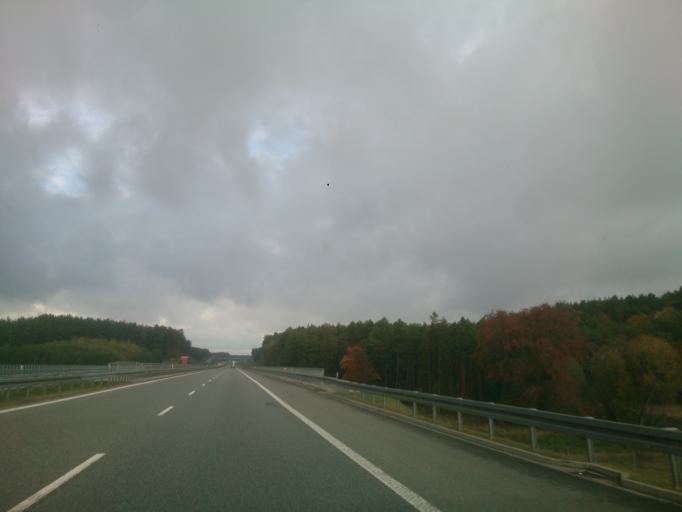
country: PL
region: Pomeranian Voivodeship
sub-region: Powiat tczewski
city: Pelplin
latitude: 53.9807
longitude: 18.6586
